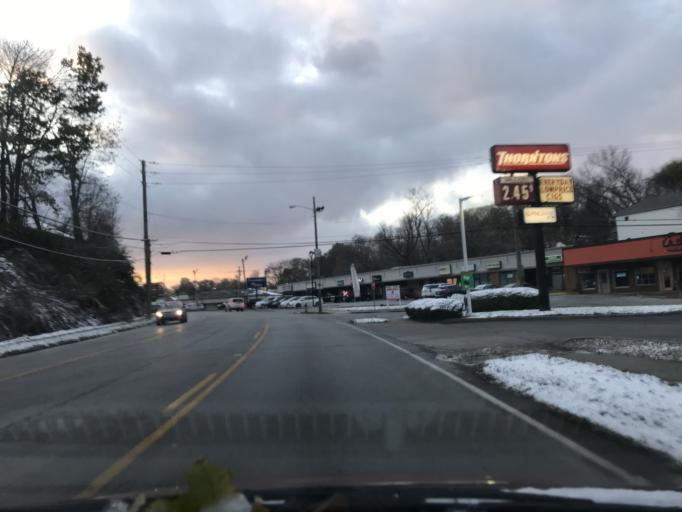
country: US
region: Indiana
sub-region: Clark County
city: Jeffersonville
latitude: 38.2596
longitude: -85.7071
